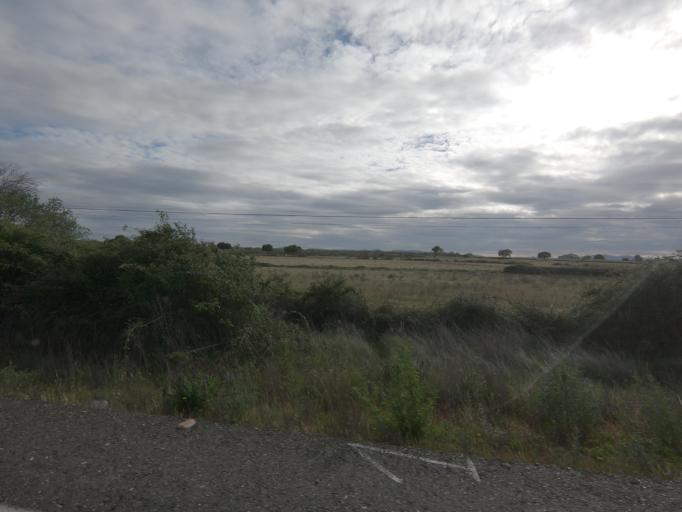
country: ES
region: Extremadura
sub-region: Provincia de Caceres
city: Moraleja
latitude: 40.0540
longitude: -6.6428
